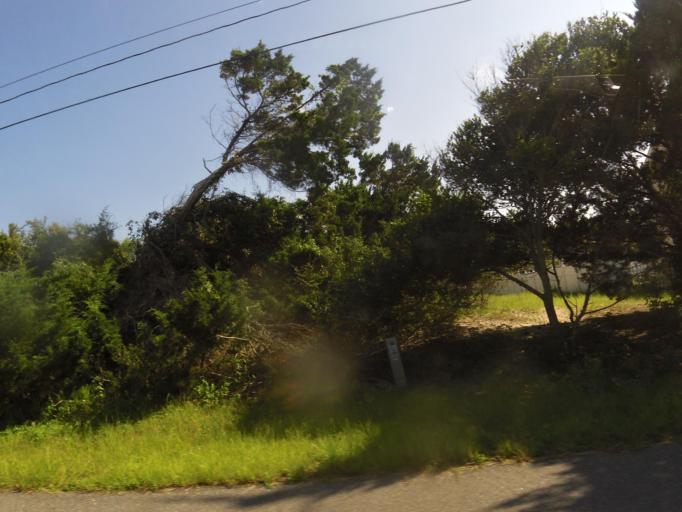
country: US
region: Florida
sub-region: Nassau County
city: Fernandina Beach
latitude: 30.6907
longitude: -81.4302
